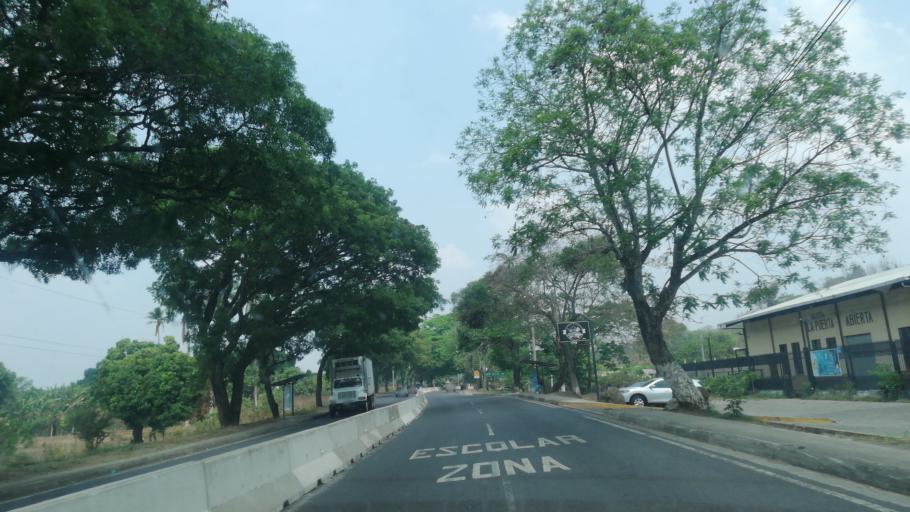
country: SV
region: Santa Ana
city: Santa Ana
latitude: 13.9768
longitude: -89.5907
